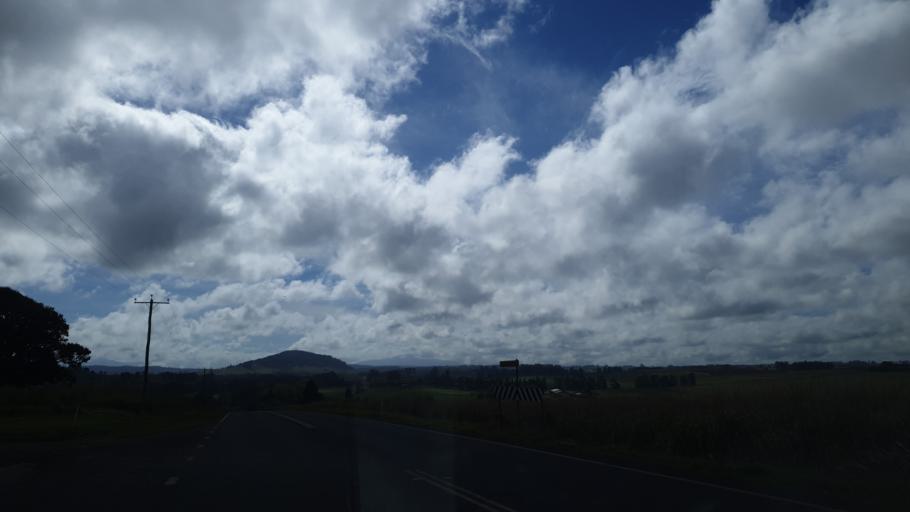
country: AU
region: Queensland
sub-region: Tablelands
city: Atherton
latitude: -17.2934
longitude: 145.5266
